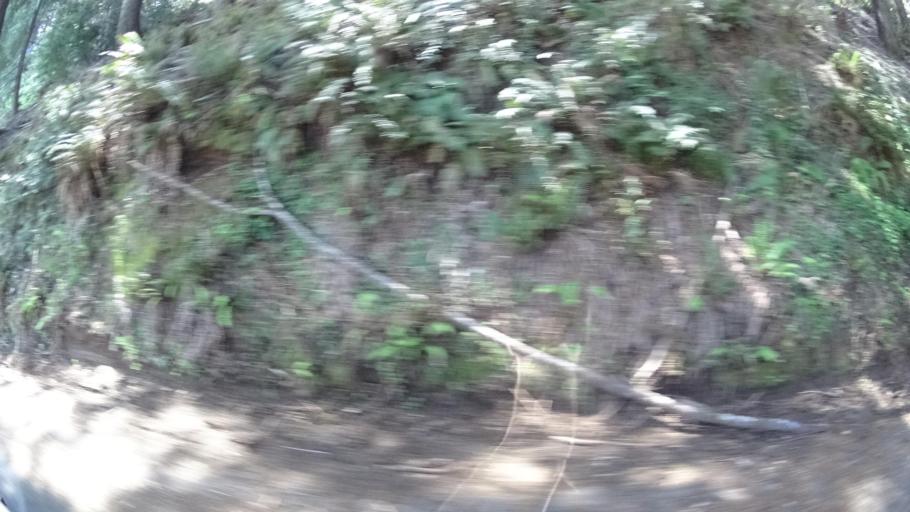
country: US
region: California
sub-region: Humboldt County
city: Redway
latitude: 40.1458
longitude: -124.0144
